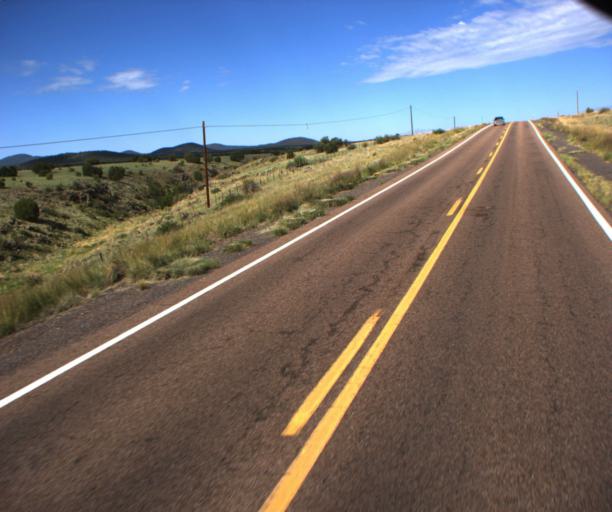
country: US
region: Arizona
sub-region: Navajo County
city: Pinetop-Lakeside
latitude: 34.2705
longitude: -109.6436
